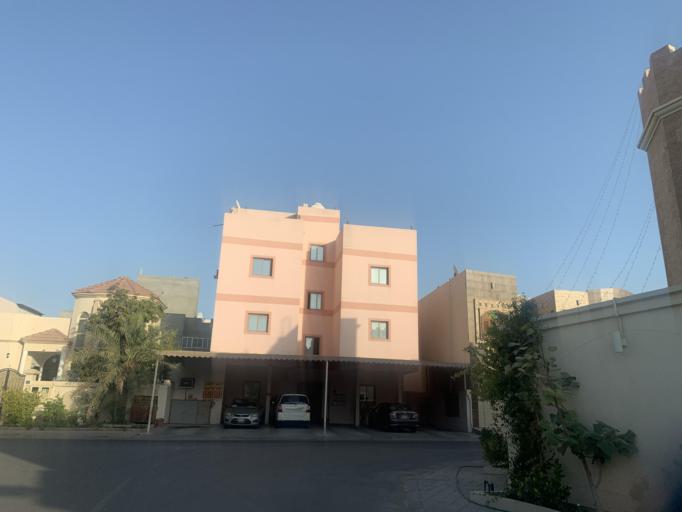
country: BH
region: Northern
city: Madinat `Isa
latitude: 26.1915
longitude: 50.4806
